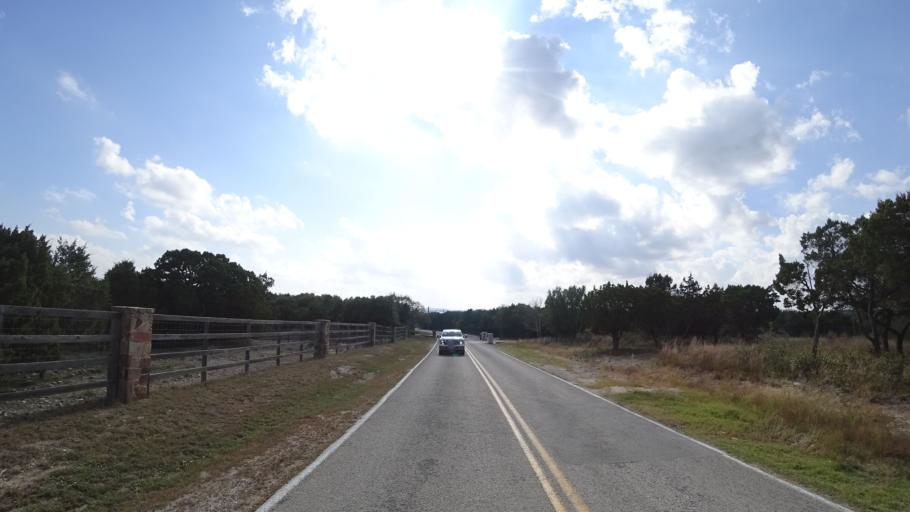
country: US
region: Texas
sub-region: Travis County
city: Barton Creek
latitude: 30.3109
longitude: -97.8655
